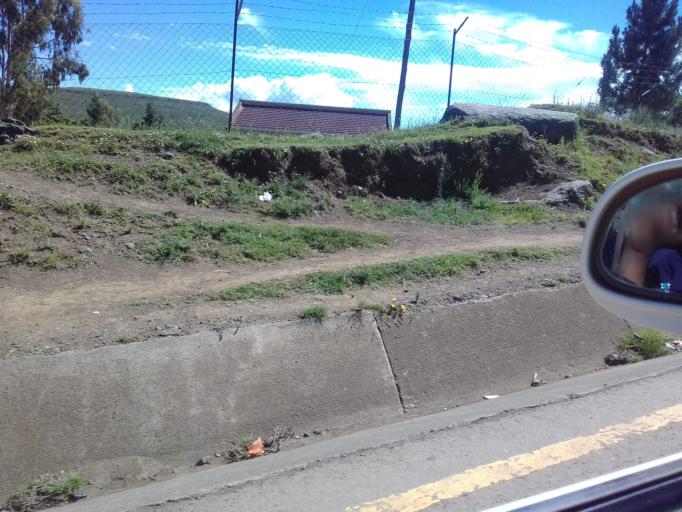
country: LS
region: Thaba-Tseka
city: Thaba-Tseka
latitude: -29.5156
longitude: 28.5927
